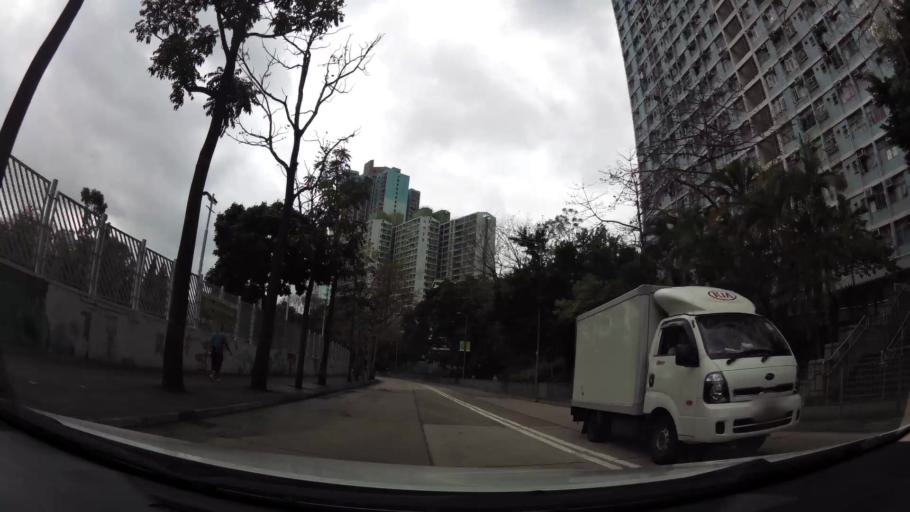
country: HK
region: Wong Tai Sin
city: Wong Tai Sin
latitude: 22.3396
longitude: 114.1894
